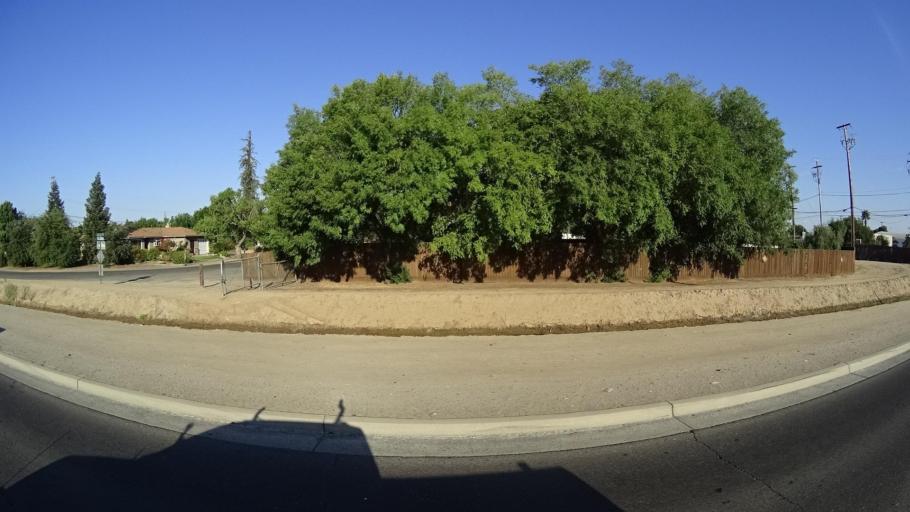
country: US
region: California
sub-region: Fresno County
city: Tarpey Village
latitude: 36.8010
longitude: -119.7005
